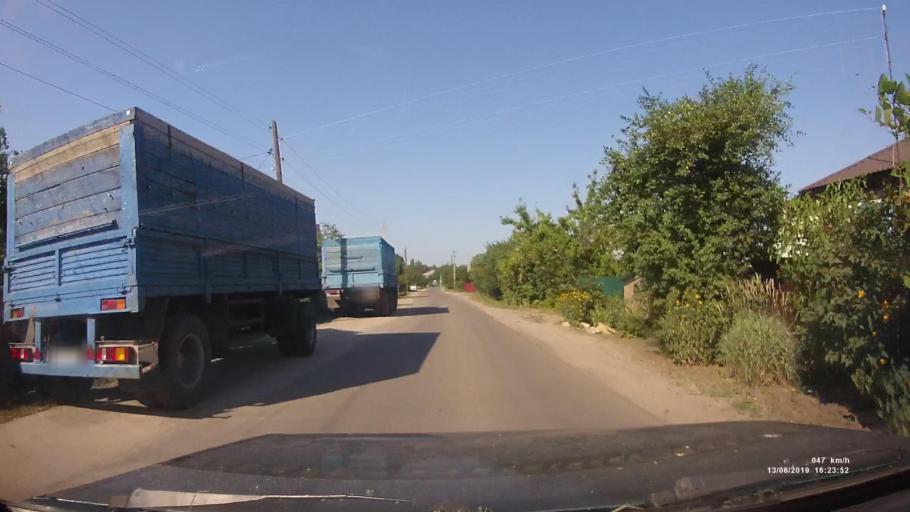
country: RU
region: Rostov
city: Kazanskaya
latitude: 49.7960
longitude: 41.1436
